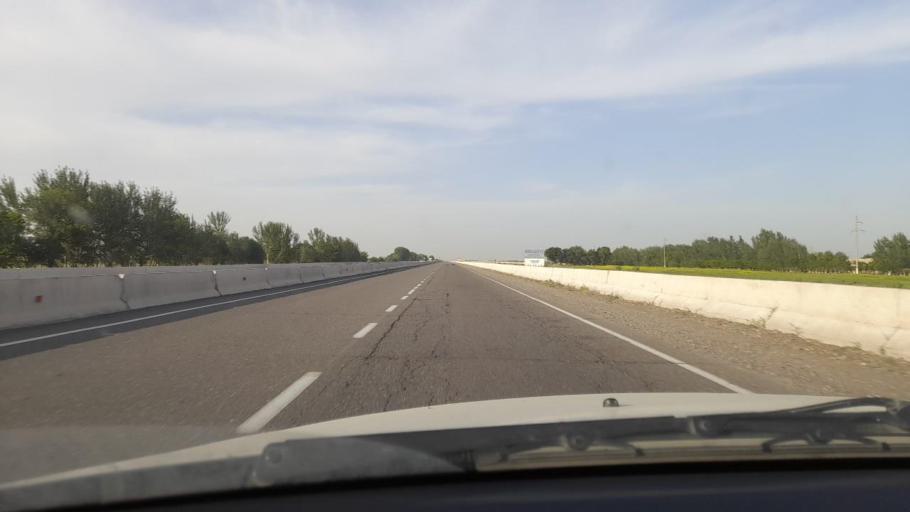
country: UZ
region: Jizzax
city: Paxtakor
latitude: 40.3258
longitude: 68.1018
